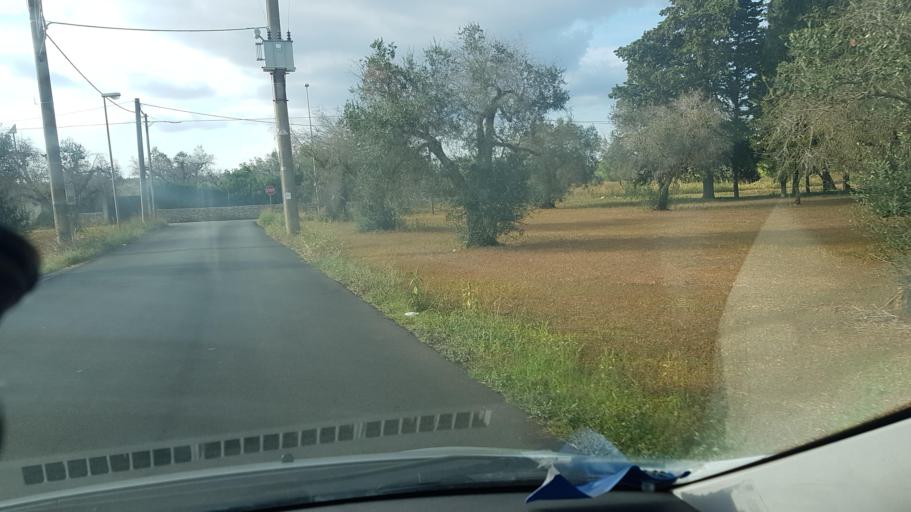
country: IT
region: Apulia
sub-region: Provincia di Brindisi
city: Cellino San Marco
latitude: 40.4633
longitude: 17.9598
